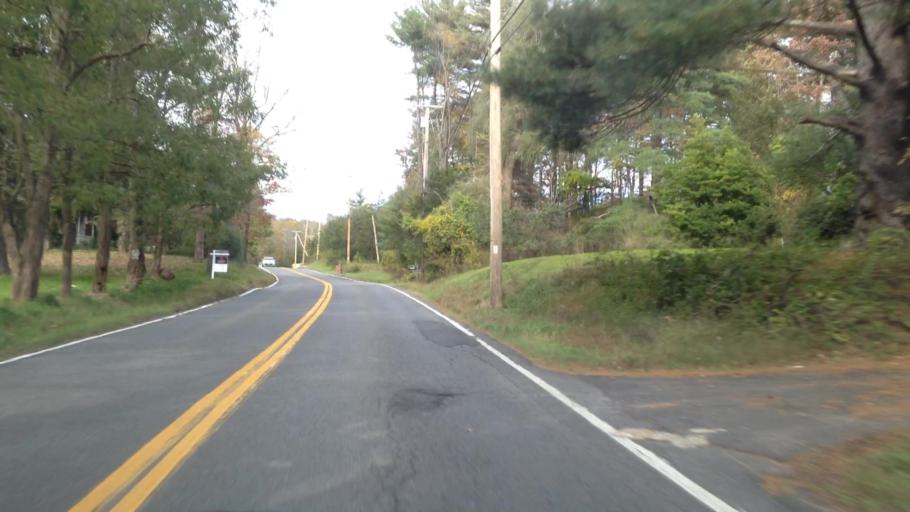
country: US
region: New York
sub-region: Ulster County
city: Rosendale Village
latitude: 41.8540
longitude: -74.0342
